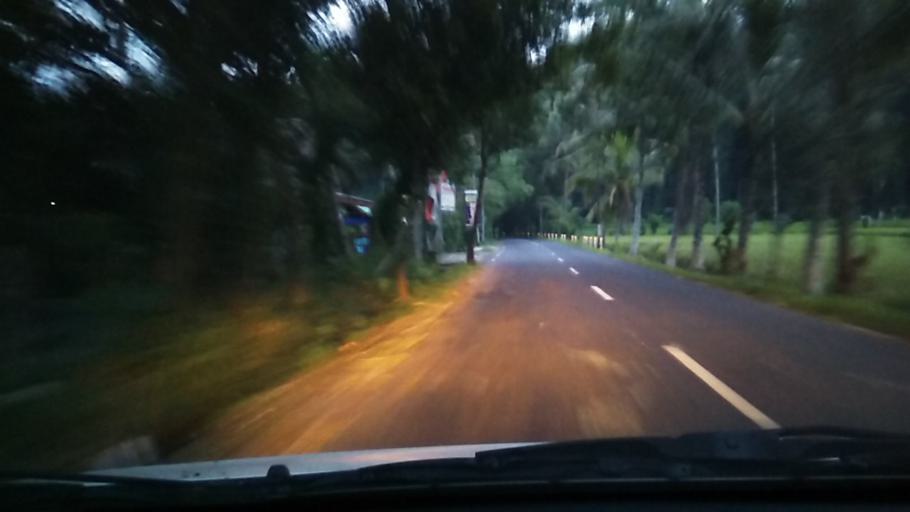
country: ID
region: Bali
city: Brahmana
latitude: -8.4775
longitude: 115.2080
